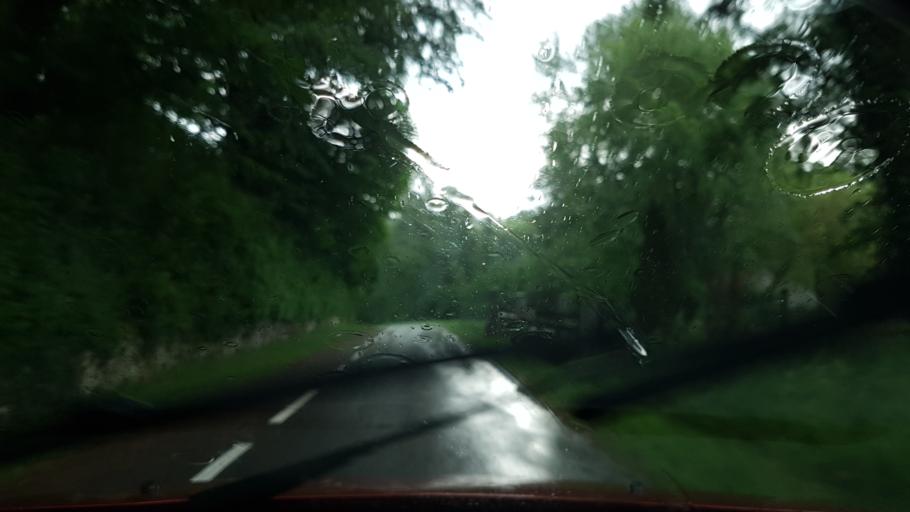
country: FR
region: Franche-Comte
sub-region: Departement du Jura
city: Clairvaux-les-Lacs
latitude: 46.5806
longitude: 5.6964
